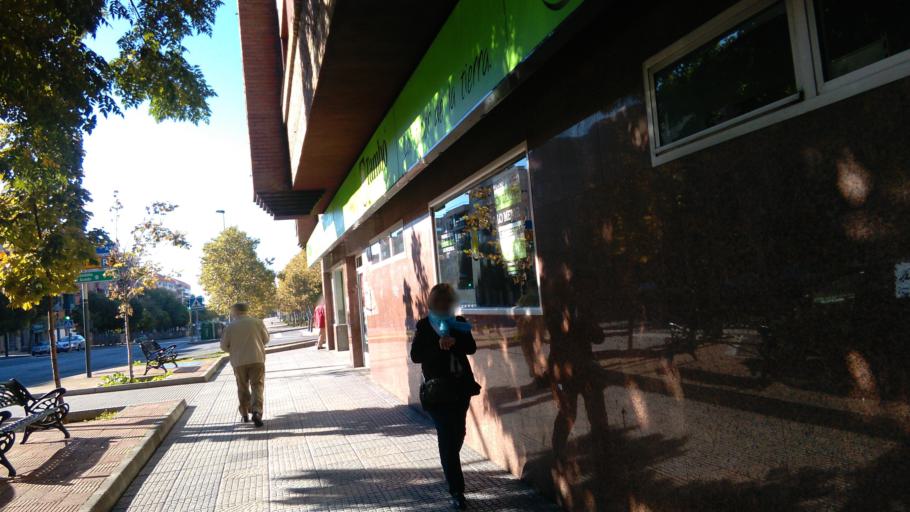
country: ES
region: Extremadura
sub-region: Provincia de Caceres
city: Caceres
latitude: 39.4659
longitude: -6.3811
